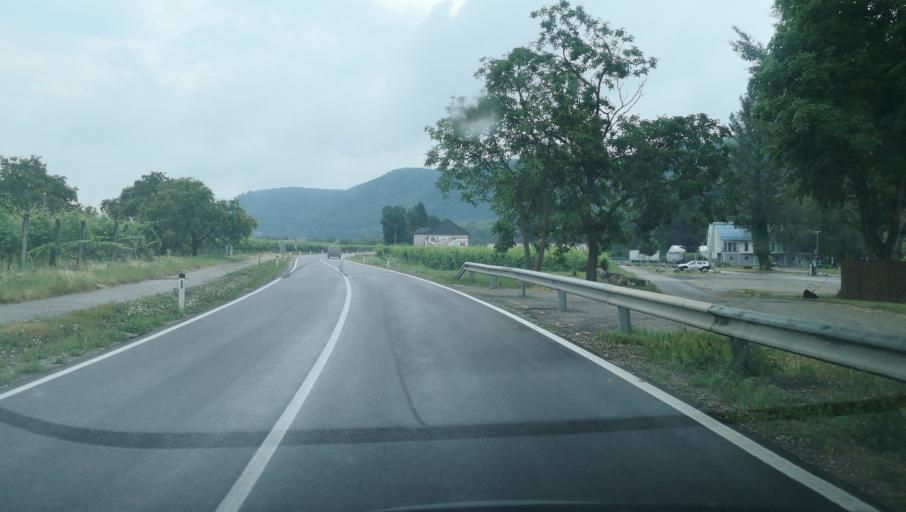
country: AT
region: Lower Austria
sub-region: Politischer Bezirk Krems
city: Durnstein
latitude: 48.3896
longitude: 15.5235
